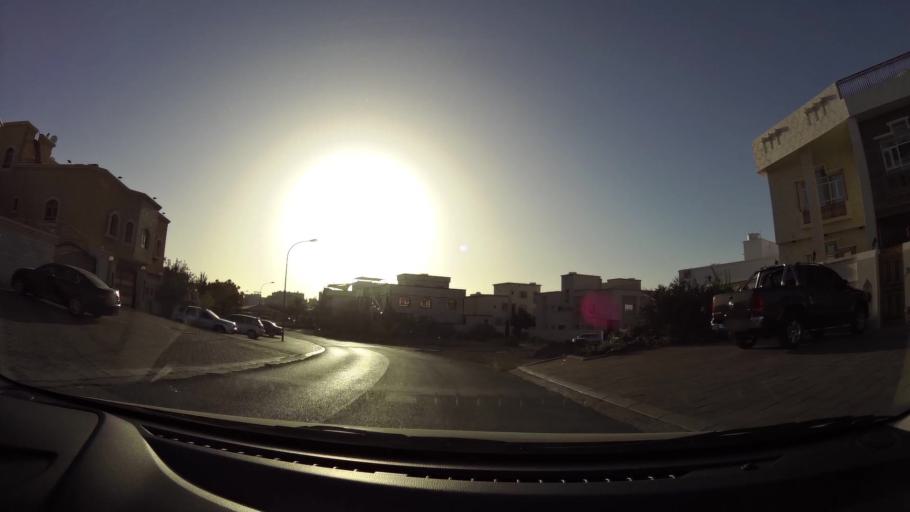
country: OM
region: Muhafazat Masqat
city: As Sib al Jadidah
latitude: 23.6092
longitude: 58.2307
